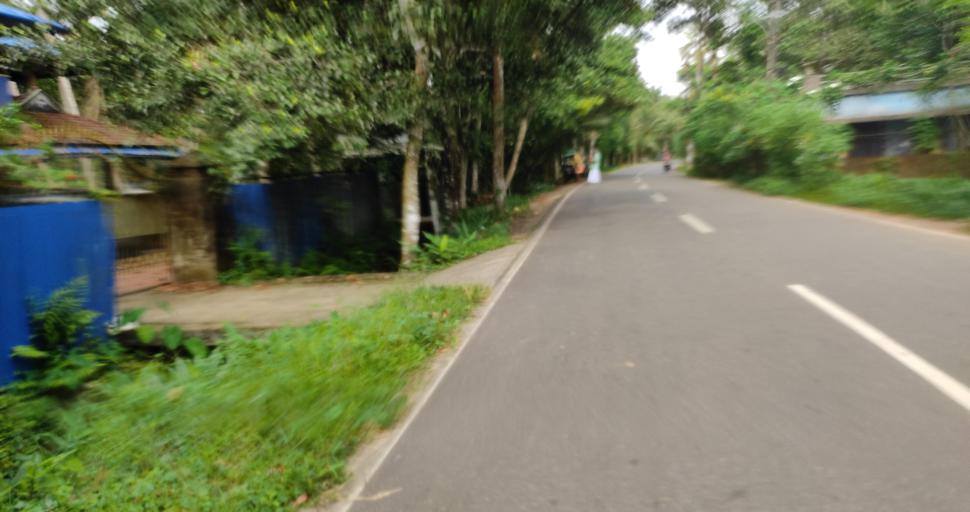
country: IN
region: Kerala
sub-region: Alappuzha
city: Vayalar
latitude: 9.6548
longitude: 76.3077
